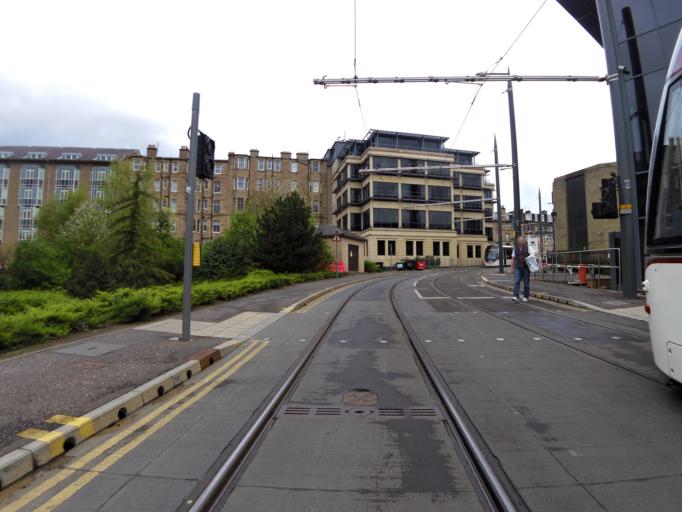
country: GB
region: Scotland
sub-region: Edinburgh
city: Edinburgh
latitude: 55.9452
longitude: -3.2216
